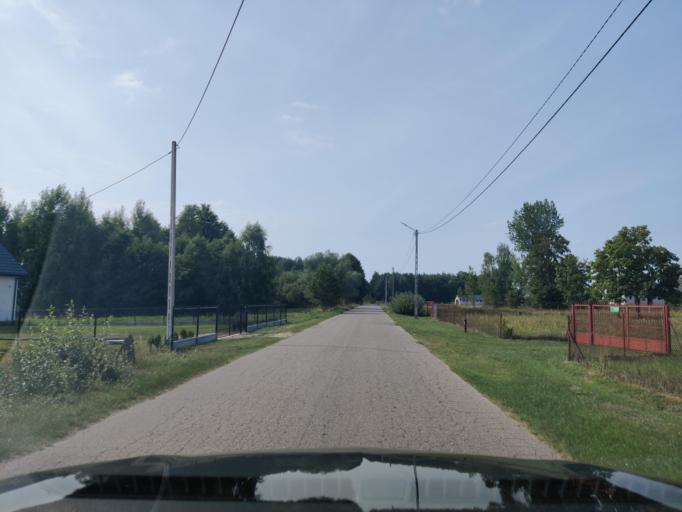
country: PL
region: Masovian Voivodeship
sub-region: Powiat wyszkowski
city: Rzasnik
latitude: 52.7412
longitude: 21.3251
